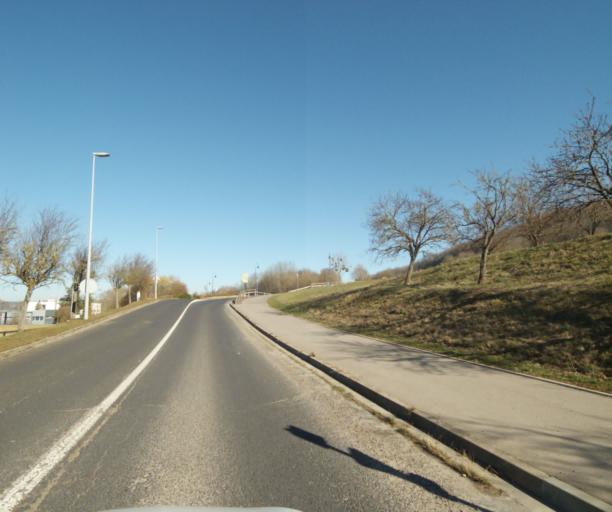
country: FR
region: Lorraine
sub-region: Departement de Meurthe-et-Moselle
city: Malzeville
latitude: 48.7306
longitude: 6.1826
